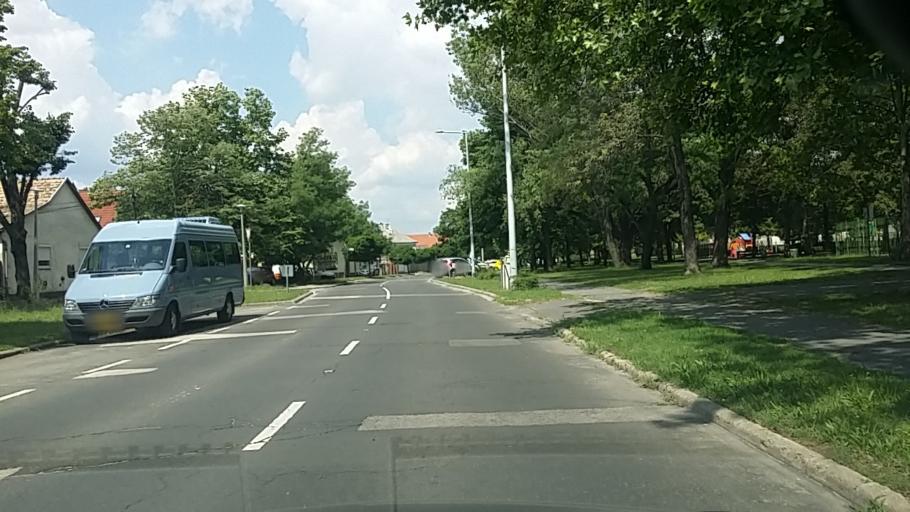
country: HU
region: Budapest
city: Budapest XV. keruelet
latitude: 47.5419
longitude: 19.1355
